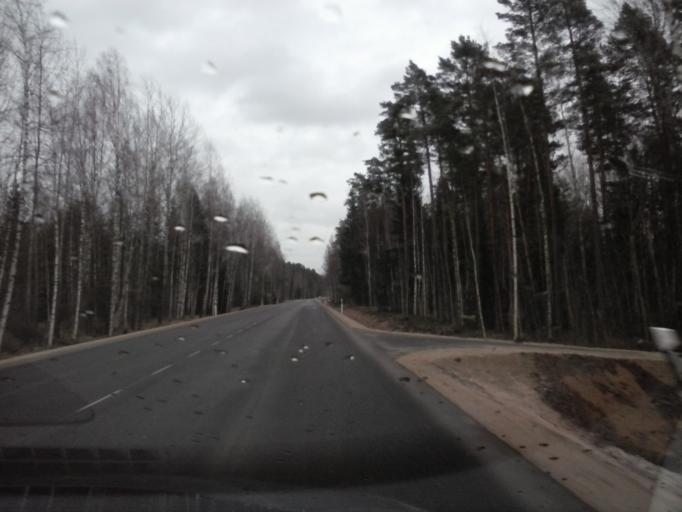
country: EE
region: Polvamaa
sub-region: Raepina vald
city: Rapina
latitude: 57.9639
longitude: 27.4864
